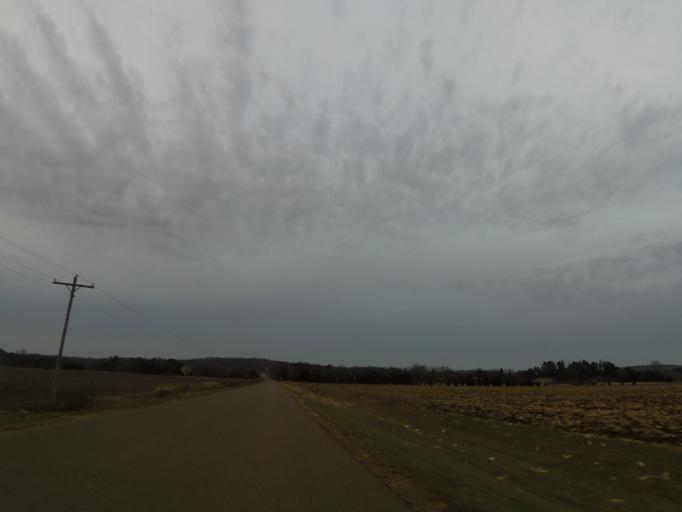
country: US
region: Wisconsin
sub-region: Pierce County
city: River Falls
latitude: 44.8852
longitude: -92.5984
